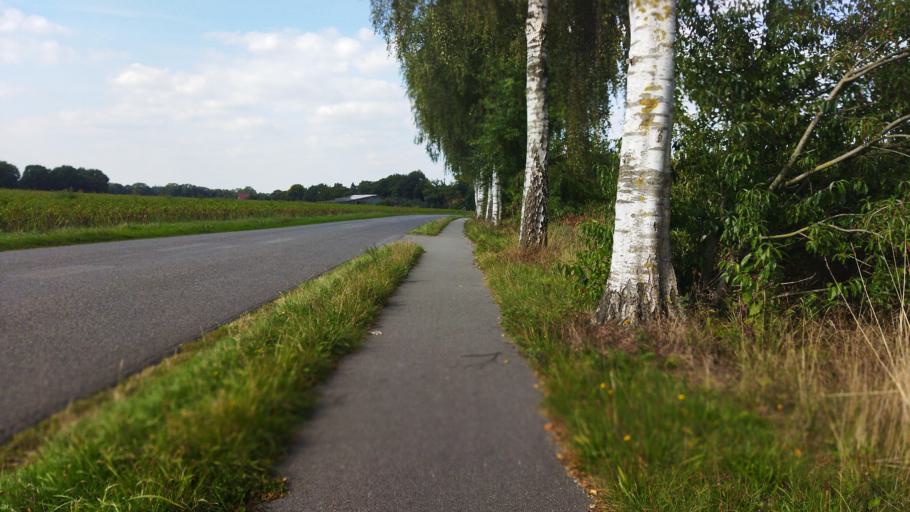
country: DE
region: Lower Saxony
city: Haren
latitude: 52.8103
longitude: 7.2595
